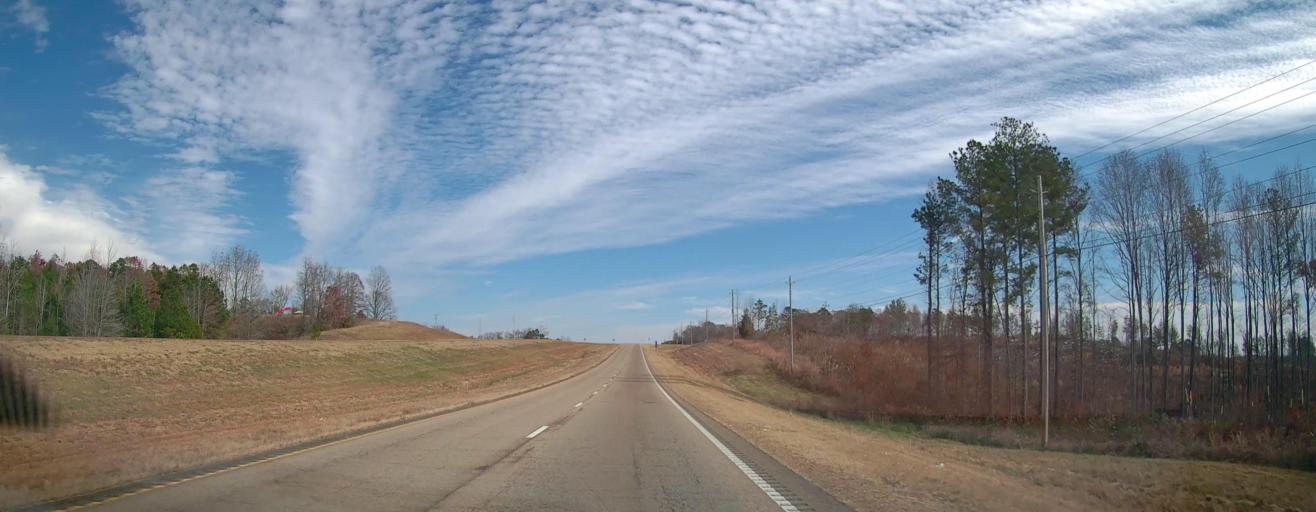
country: US
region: Mississippi
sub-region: Alcorn County
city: Corinth
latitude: 34.9310
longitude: -88.6999
